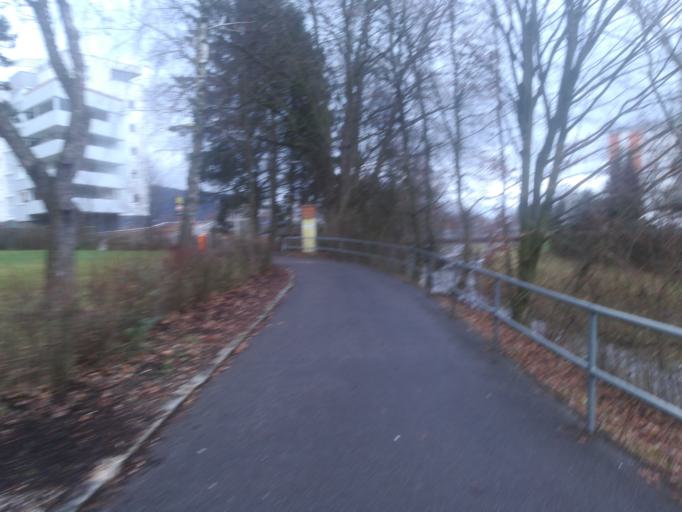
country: AT
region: Upper Austria
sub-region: Linz Stadt
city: Linz
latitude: 48.3298
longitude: 14.3107
